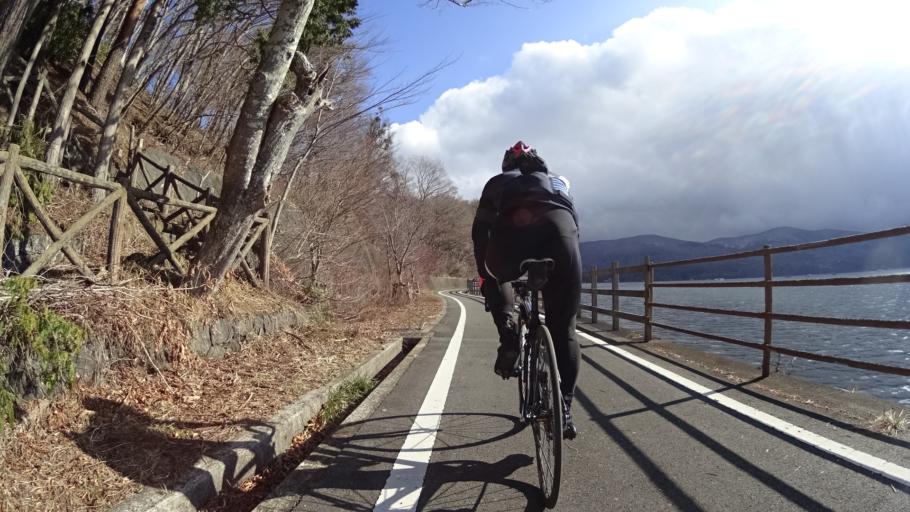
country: JP
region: Shizuoka
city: Gotemba
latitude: 35.4238
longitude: 138.8807
